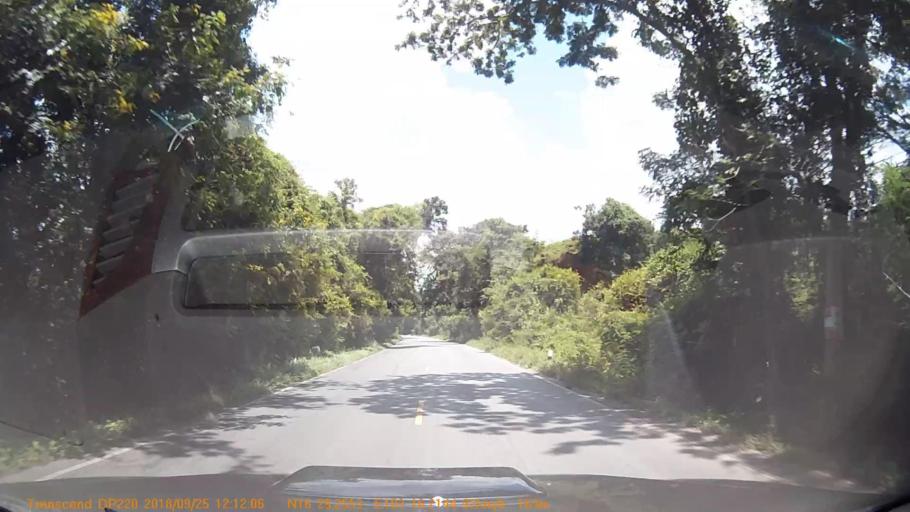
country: TH
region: Kalasin
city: Huai Mek
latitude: 16.4878
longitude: 103.2703
